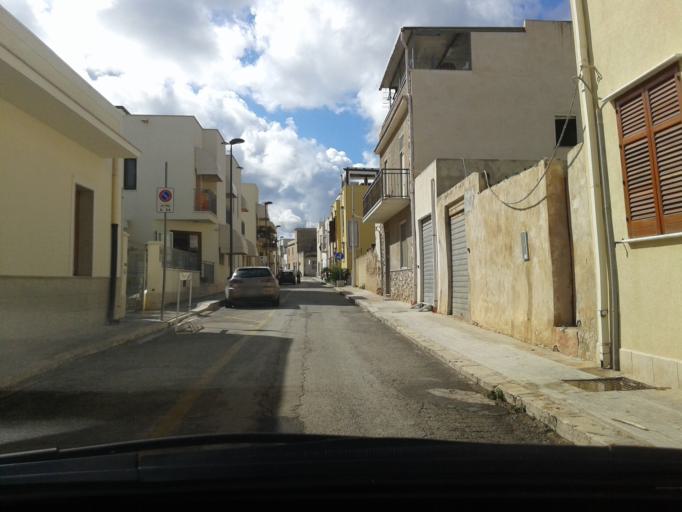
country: IT
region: Sicily
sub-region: Trapani
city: San Vito Lo Capo
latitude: 38.1747
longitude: 12.7382
